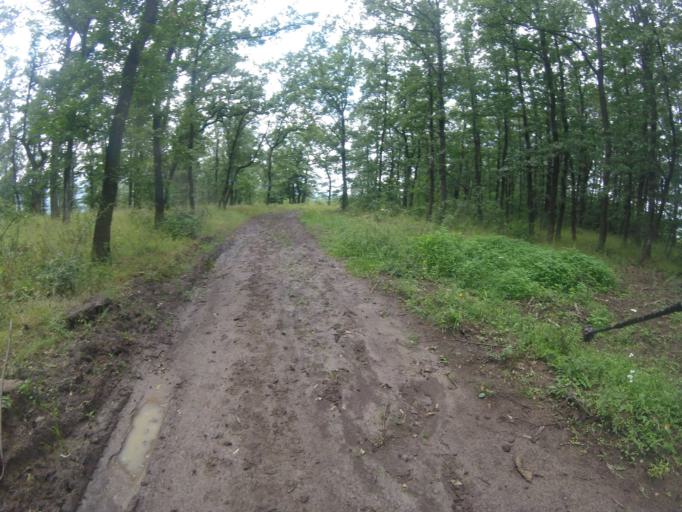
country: SK
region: Nitriansky
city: Sahy
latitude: 48.0232
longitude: 18.9723
